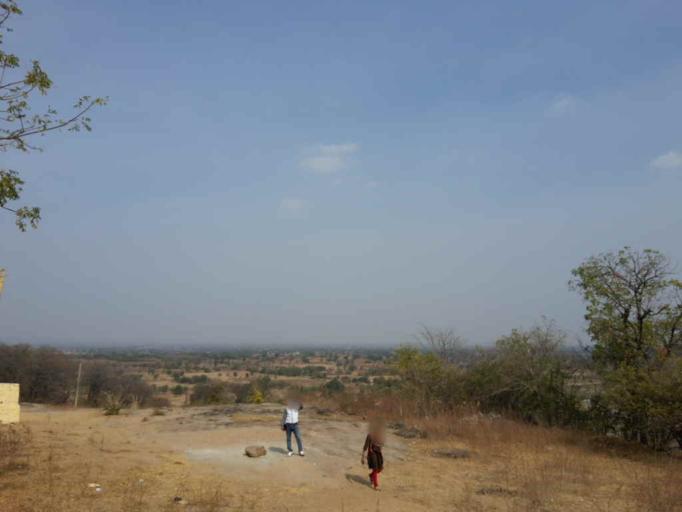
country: IN
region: Telangana
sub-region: Karimnagar
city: Sirsilla
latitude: 18.4462
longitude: 78.7661
